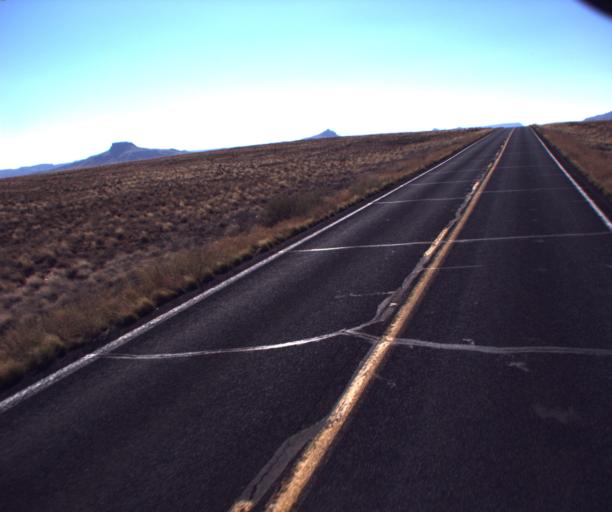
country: US
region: Arizona
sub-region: Navajo County
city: First Mesa
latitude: 35.6212
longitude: -110.4786
